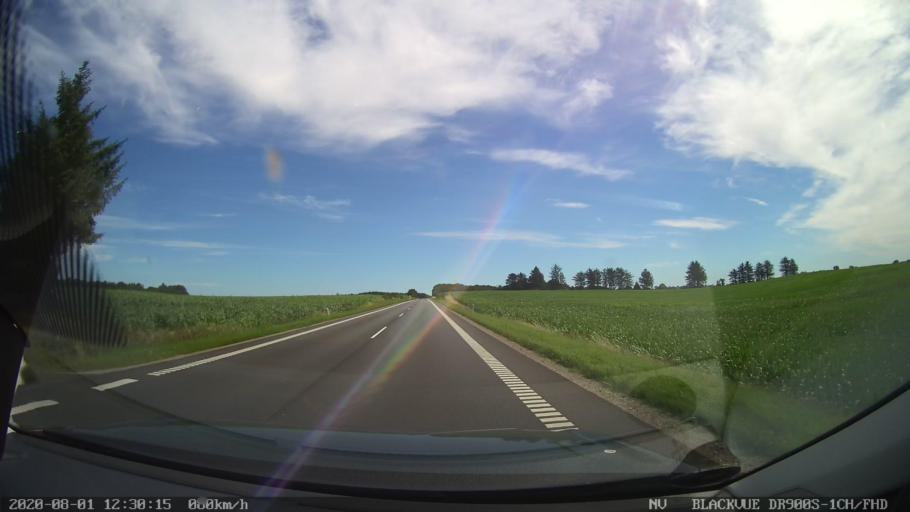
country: DK
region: Central Jutland
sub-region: Viborg Kommune
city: Stoholm
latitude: 56.4354
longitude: 9.1371
